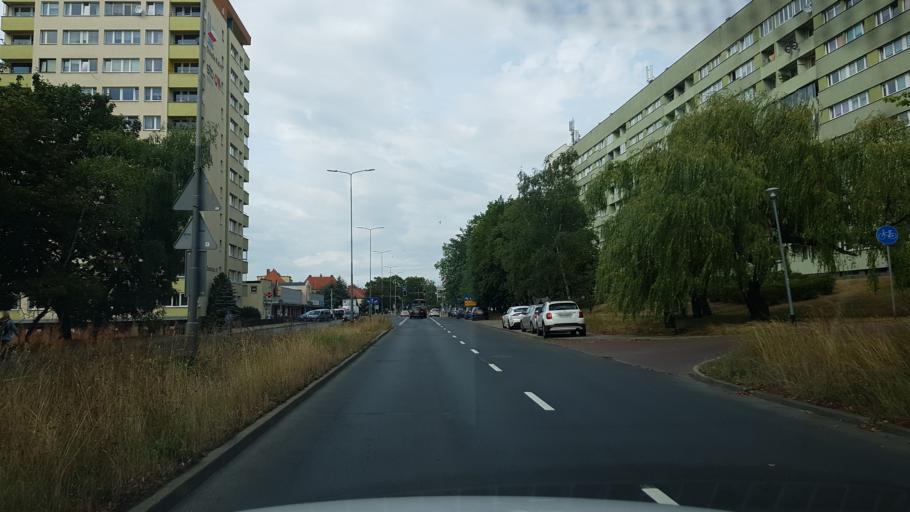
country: PL
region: West Pomeranian Voivodeship
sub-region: Szczecin
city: Szczecin
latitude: 53.4313
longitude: 14.5124
